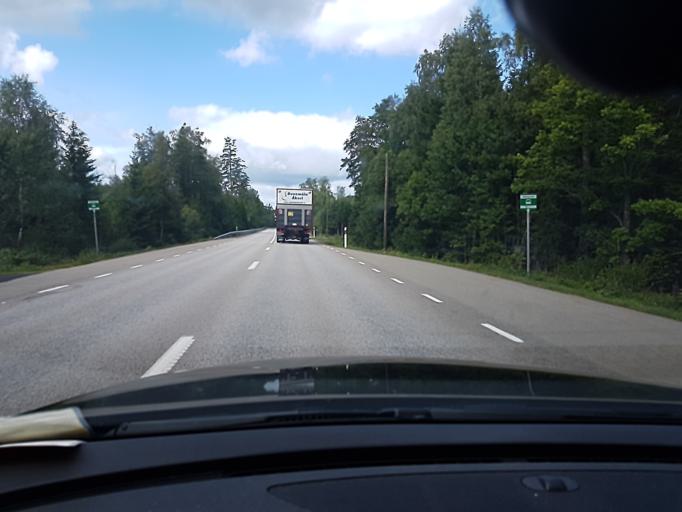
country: SE
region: Kronoberg
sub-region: Lessebo Kommun
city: Lessebo
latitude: 56.7301
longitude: 15.3099
